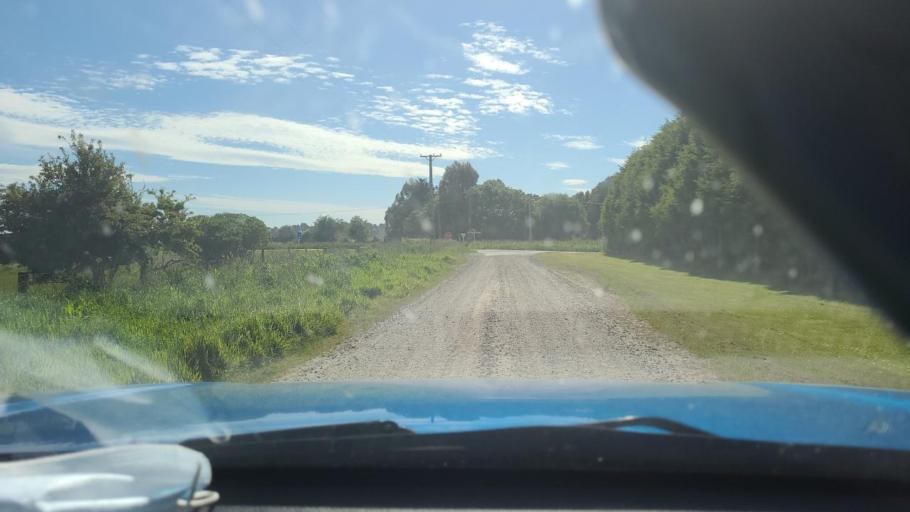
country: NZ
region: Southland
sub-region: Gore District
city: Gore
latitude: -46.4692
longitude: 168.8029
